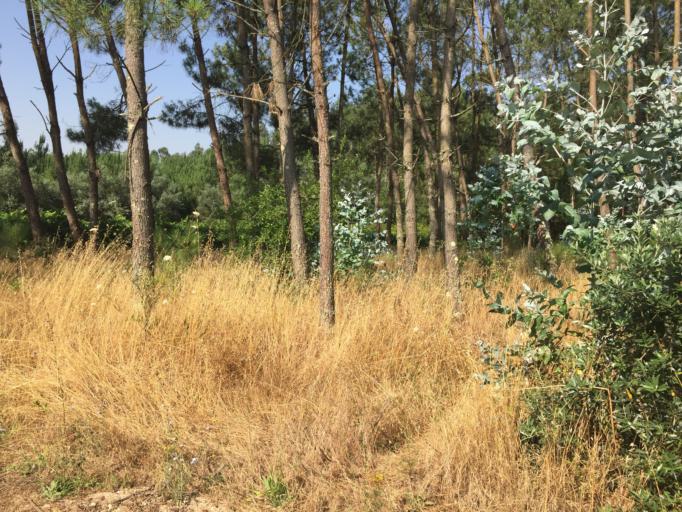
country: PT
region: Coimbra
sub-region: Cantanhede
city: Cantanhede
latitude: 40.4257
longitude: -8.5471
